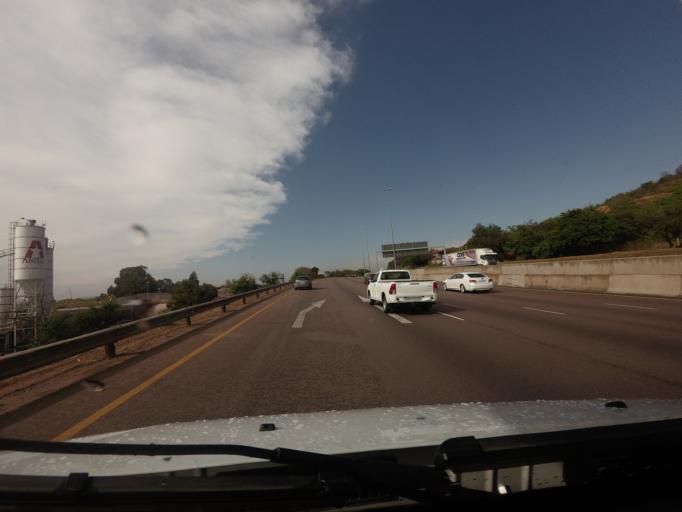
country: ZA
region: Gauteng
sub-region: City of Tshwane Metropolitan Municipality
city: Pretoria
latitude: -25.6940
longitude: 28.2828
